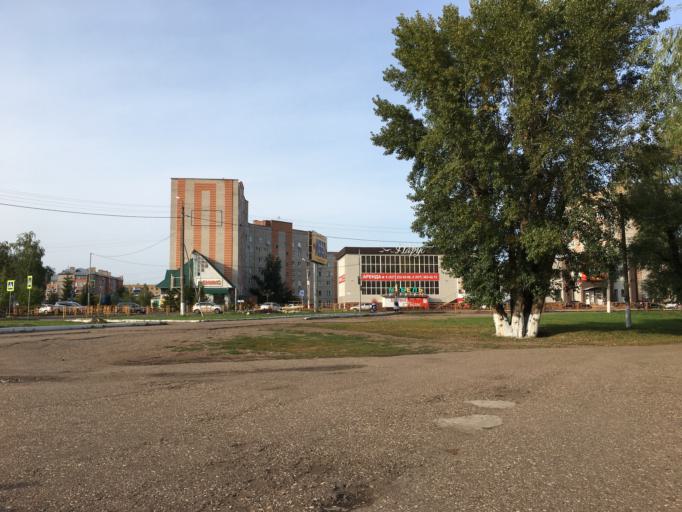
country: RU
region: Bashkortostan
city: Meleuz
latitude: 52.9594
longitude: 55.9212
